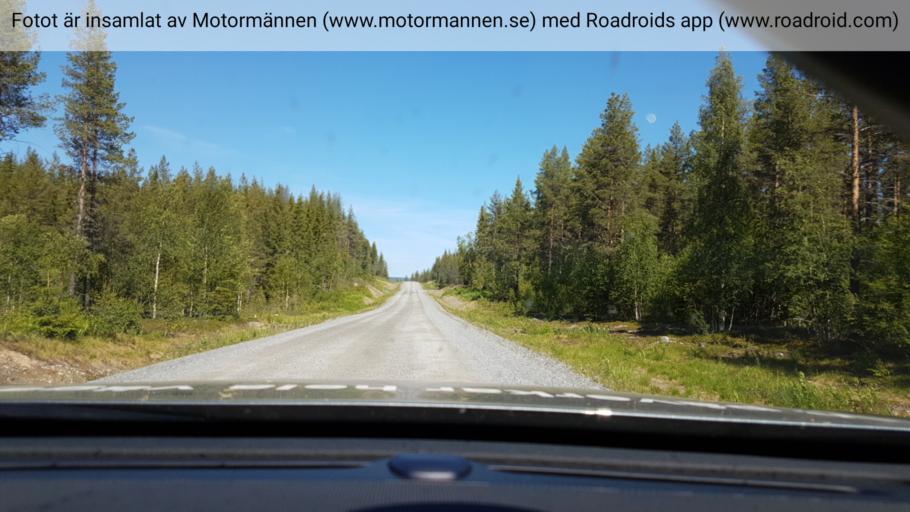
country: SE
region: Vaesterbotten
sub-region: Vilhelmina Kommun
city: Sjoberg
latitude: 64.6686
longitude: 15.7569
